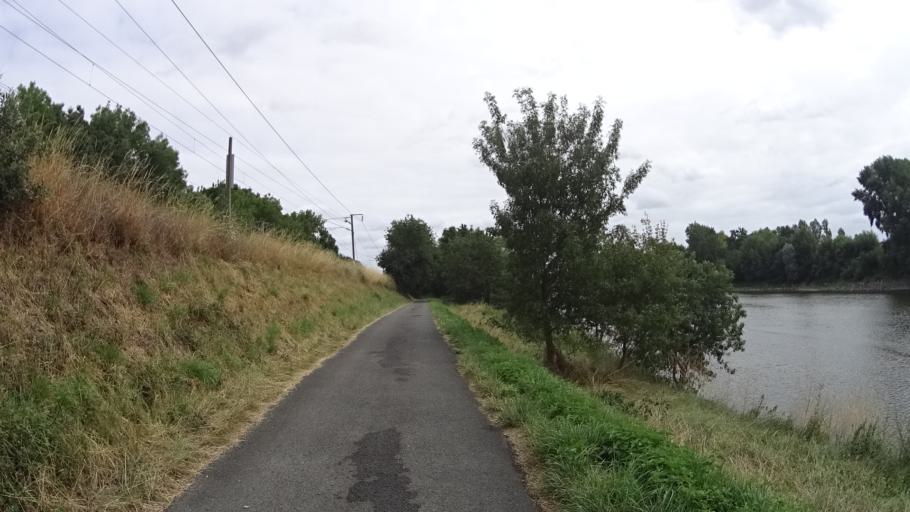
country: FR
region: Pays de la Loire
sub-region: Departement de Maine-et-Loire
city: Savennieres
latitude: 47.3904
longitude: -0.6360
